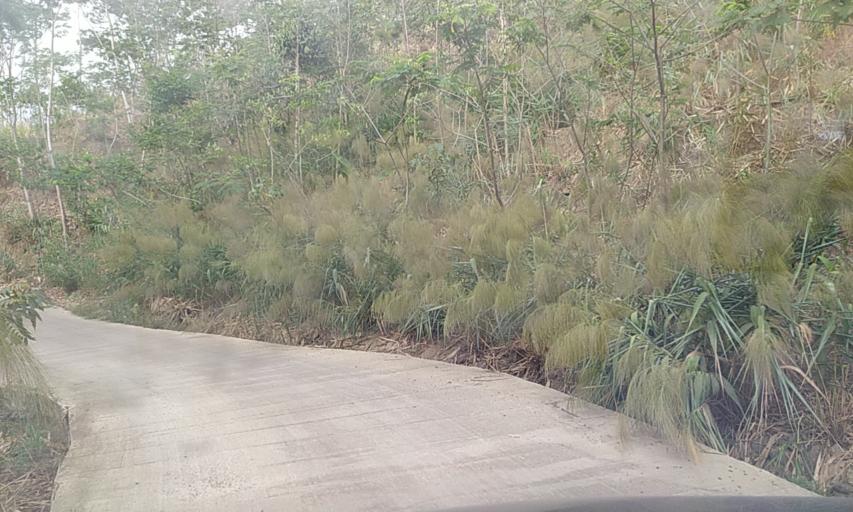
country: ID
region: Central Java
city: Randudongkal
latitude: -7.1918
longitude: 109.4140
